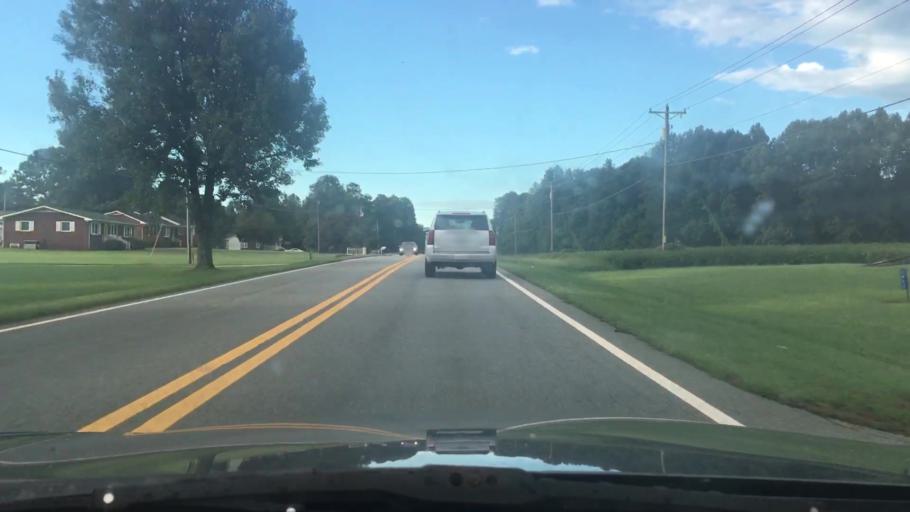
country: US
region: North Carolina
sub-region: Alamance County
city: Green Level
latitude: 36.1736
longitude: -79.3305
